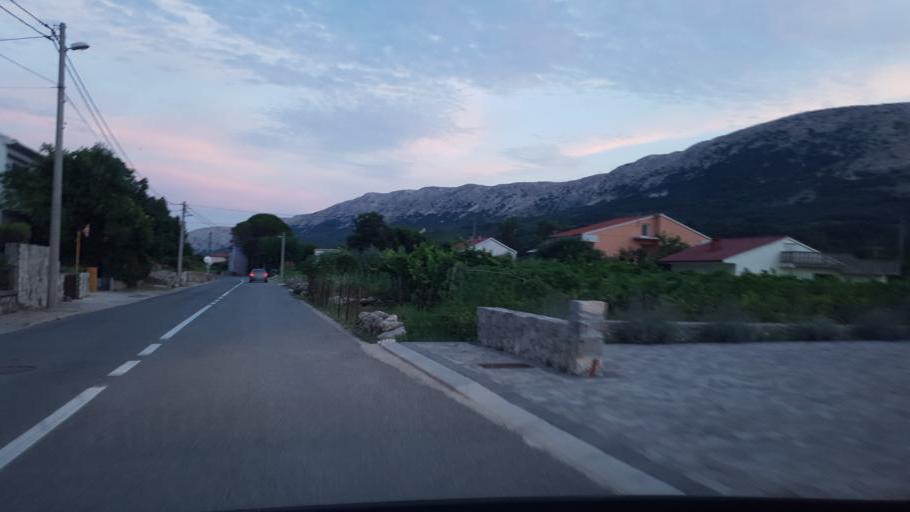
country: HR
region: Primorsko-Goranska
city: Punat
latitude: 44.9910
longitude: 14.7198
